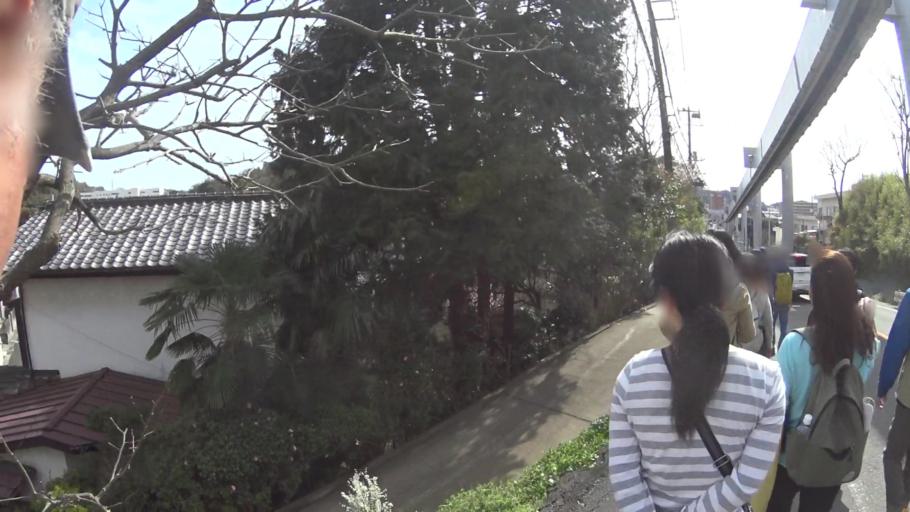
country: JP
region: Kanagawa
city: Kamakura
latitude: 35.3350
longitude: 139.5214
